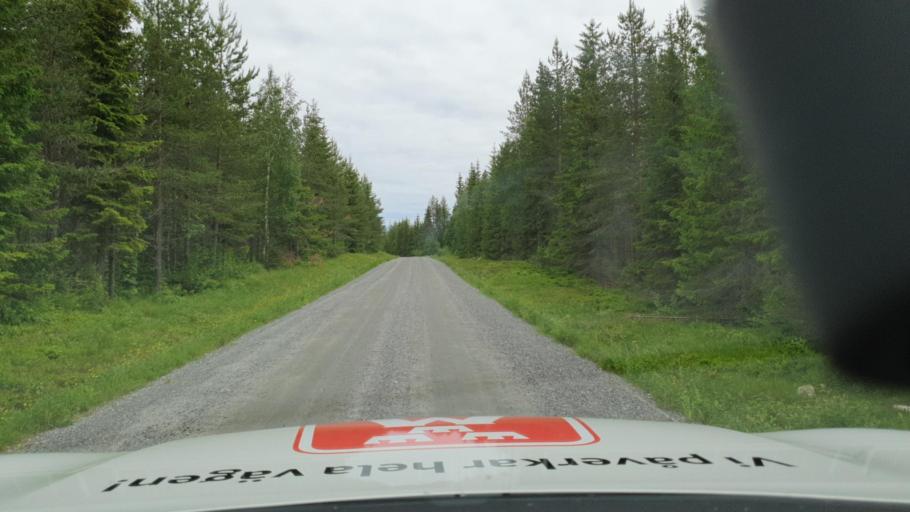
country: SE
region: Vaesterbotten
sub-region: Skelleftea Kommun
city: Langsele
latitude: 64.4797
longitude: 20.2588
